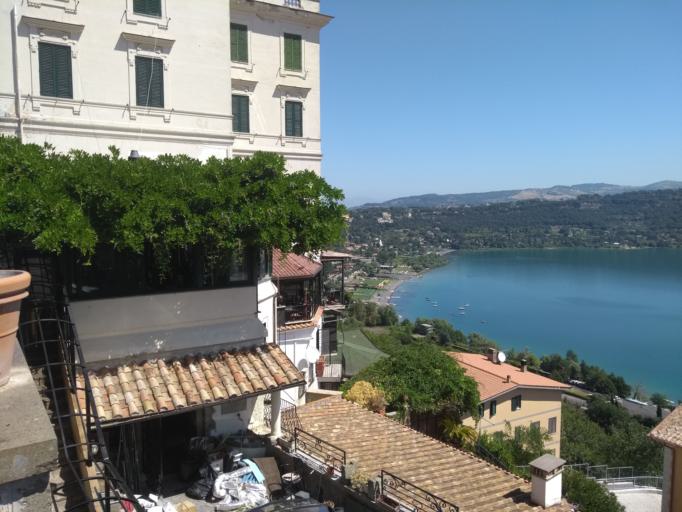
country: IT
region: Latium
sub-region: Citta metropolitana di Roma Capitale
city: Castel Gandolfo
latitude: 41.7500
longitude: 12.6486
